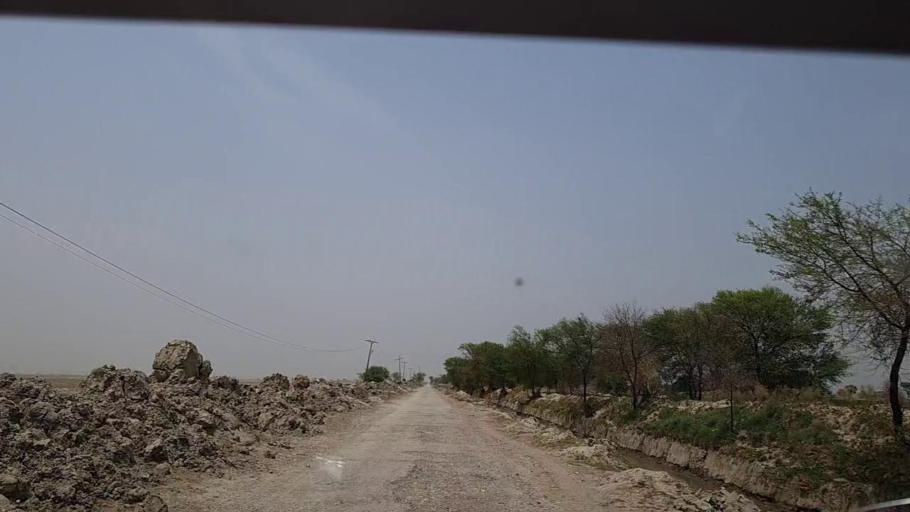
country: PK
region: Sindh
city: Khairpur Nathan Shah
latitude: 27.0443
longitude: 67.6188
